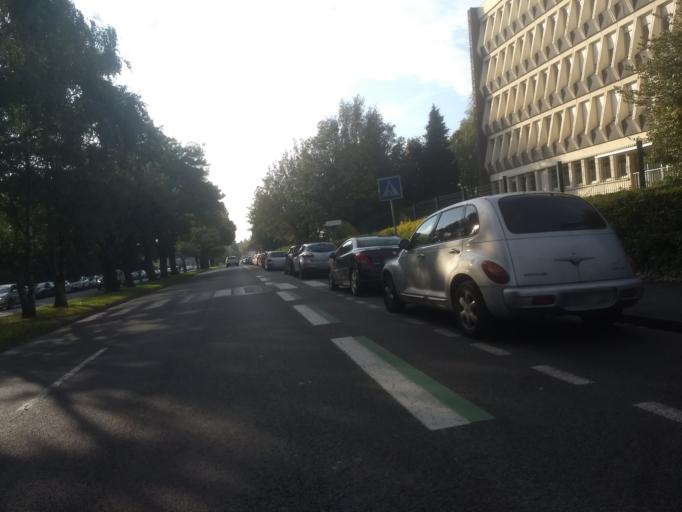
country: FR
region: Nord-Pas-de-Calais
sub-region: Departement du Pas-de-Calais
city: Sainte-Catherine
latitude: 50.2928
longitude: 2.7581
